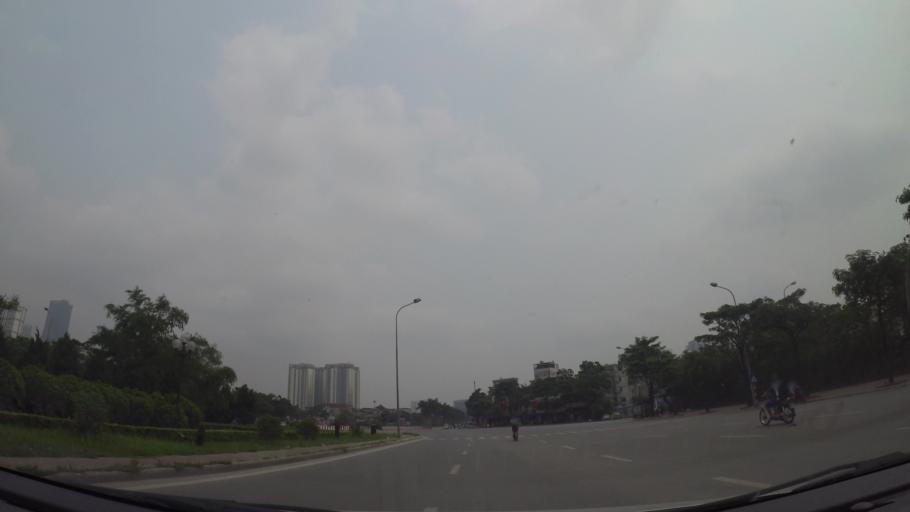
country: VN
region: Ha Noi
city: Cau Dien
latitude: 21.0159
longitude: 105.7677
